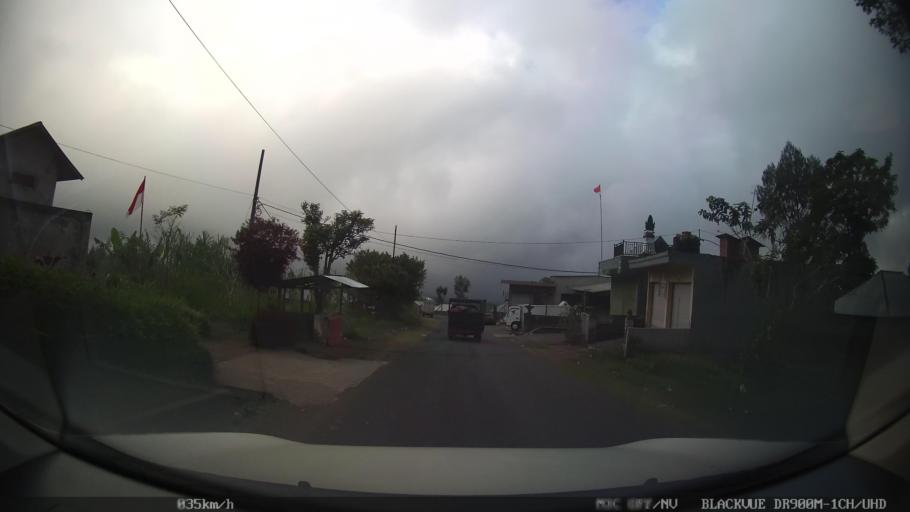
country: ID
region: Bali
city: Banjar Kedisan
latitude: -8.2678
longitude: 115.3308
